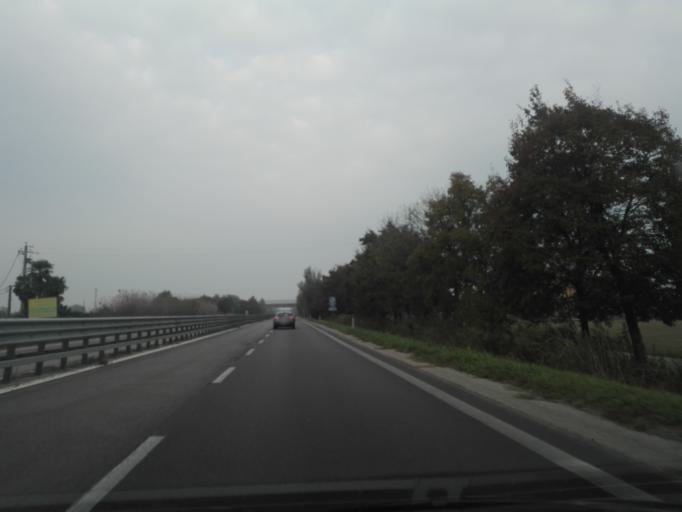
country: IT
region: Veneto
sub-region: Provincia di Verona
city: Spinimbecco
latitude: 45.1362
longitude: 11.3635
